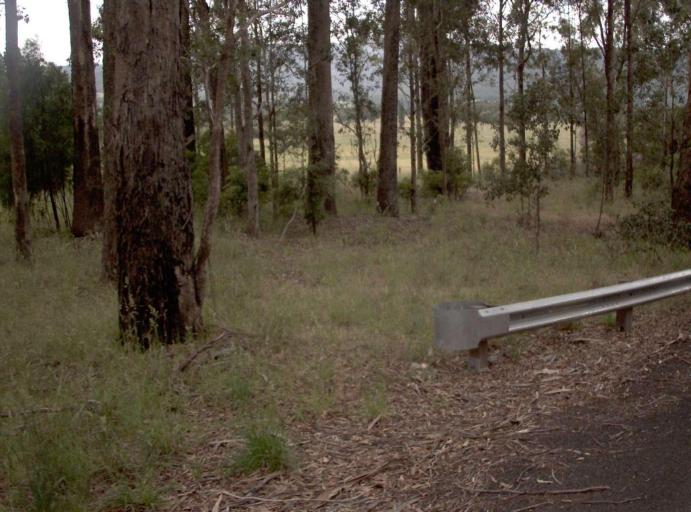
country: AU
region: New South Wales
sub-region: Bombala
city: Bombala
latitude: -37.4975
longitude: 149.1811
